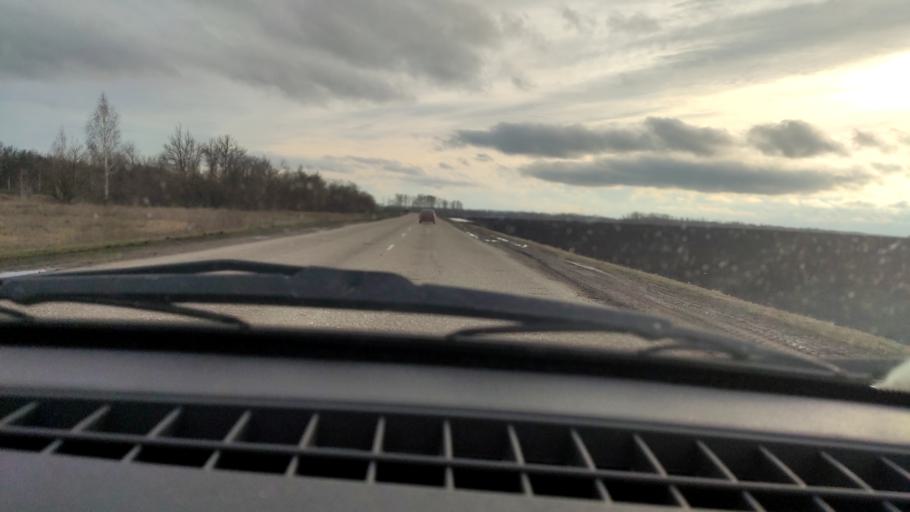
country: RU
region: Bashkortostan
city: Chishmy
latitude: 54.5464
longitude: 55.3258
